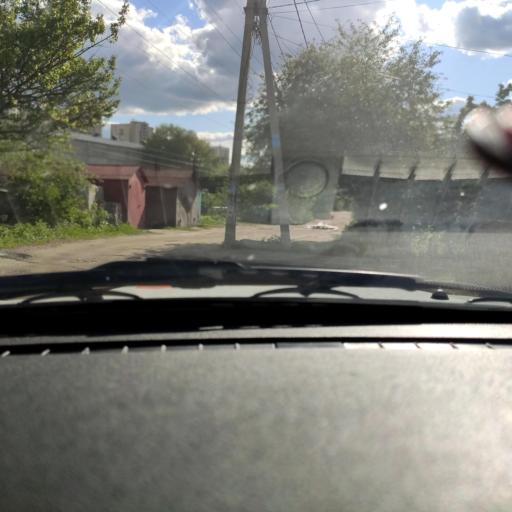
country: RU
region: Voronezj
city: Voronezh
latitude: 51.6662
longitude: 39.1609
